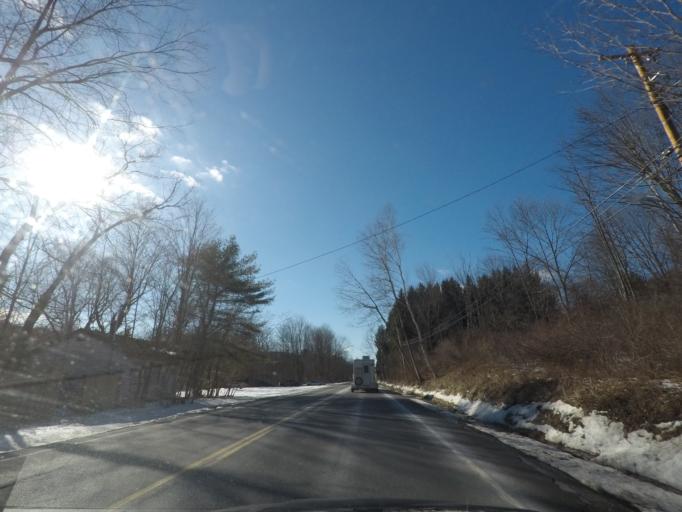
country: US
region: Massachusetts
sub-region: Berkshire County
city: Richmond
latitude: 42.4172
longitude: -73.4807
